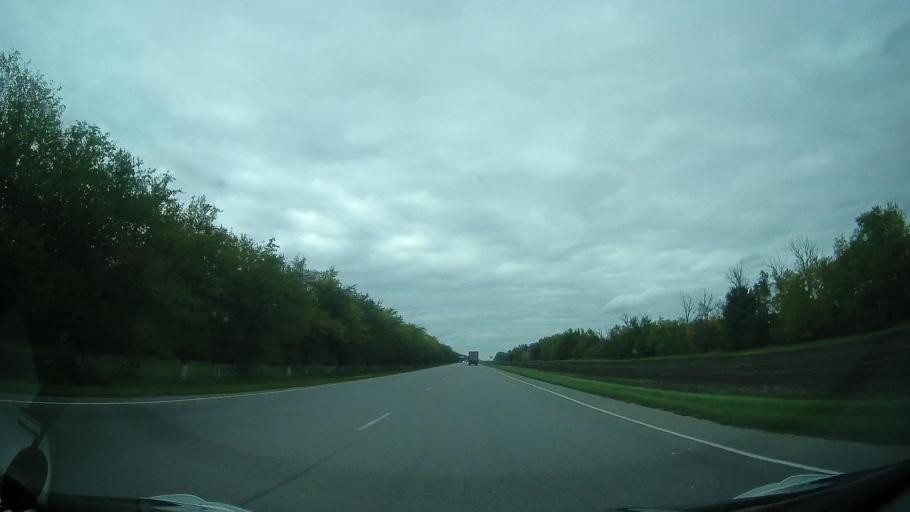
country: RU
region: Rostov
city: Yegorlykskaya
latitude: 46.6181
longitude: 40.5999
